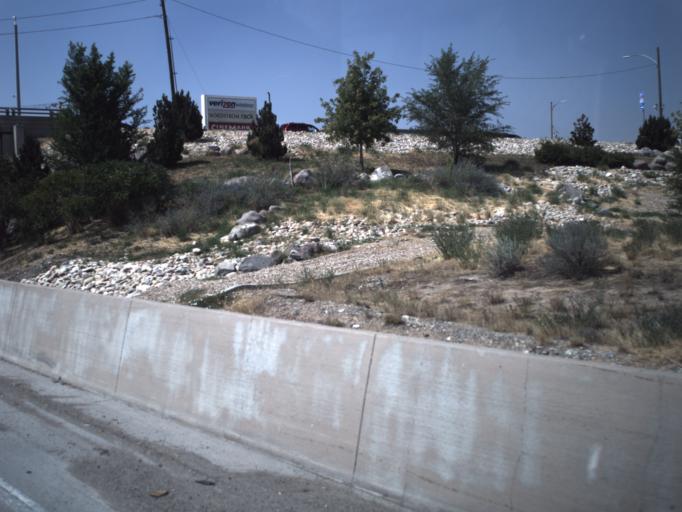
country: US
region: Utah
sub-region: Salt Lake County
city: Willard
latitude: 40.7199
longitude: -111.8529
